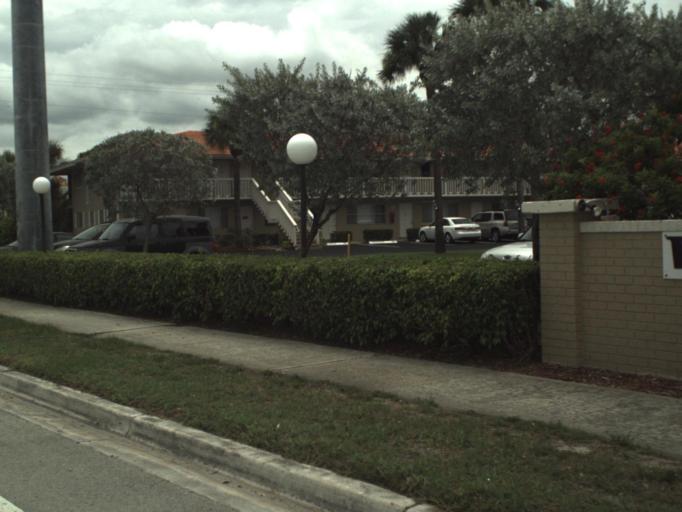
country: US
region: Florida
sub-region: Palm Beach County
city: Lake Park
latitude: 26.8095
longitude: -80.0565
